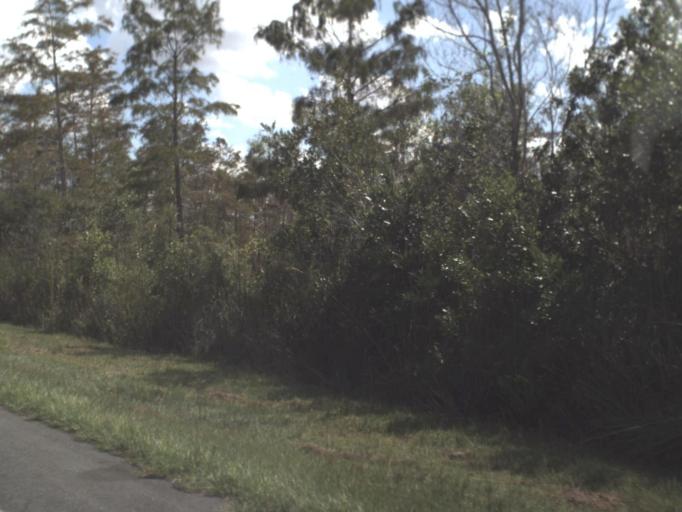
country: US
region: Florida
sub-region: Miami-Dade County
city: Kendall West
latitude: 25.8347
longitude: -80.9073
